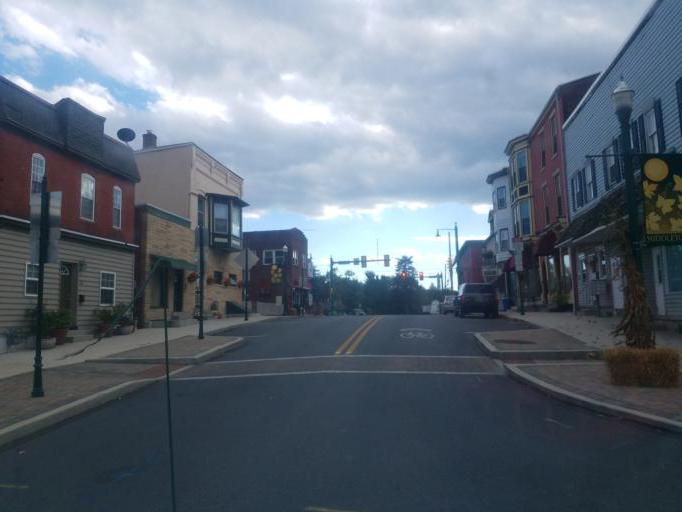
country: US
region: Pennsylvania
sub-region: Dauphin County
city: Middletown
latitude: 40.1931
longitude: -76.7319
